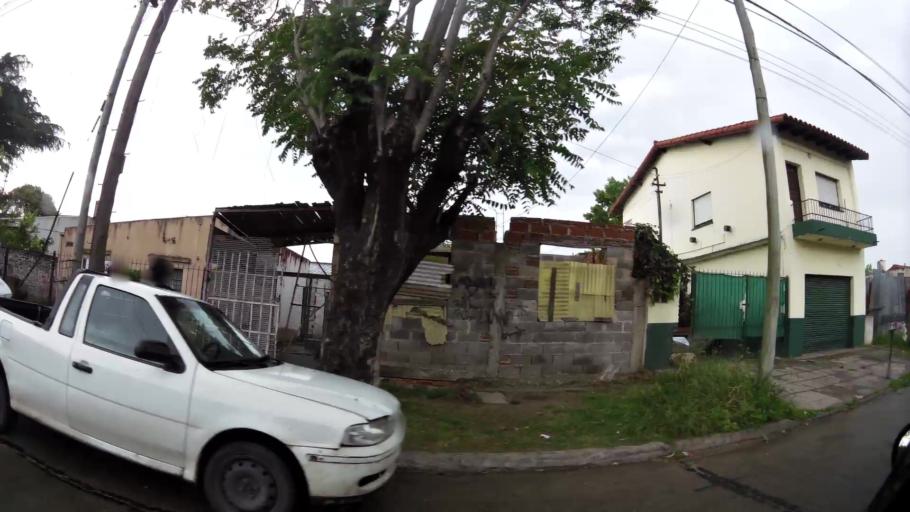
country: AR
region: Buenos Aires
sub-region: Partido de Quilmes
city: Quilmes
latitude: -34.7704
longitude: -58.2103
